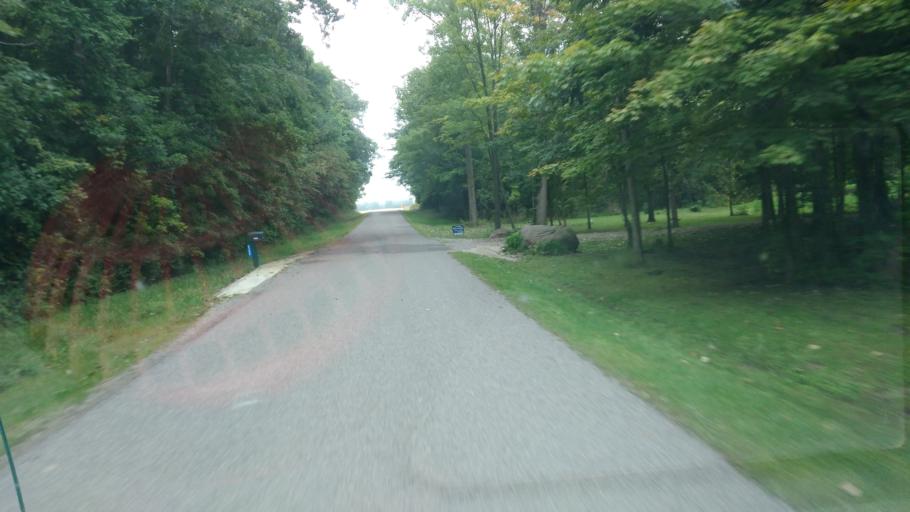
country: US
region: Ohio
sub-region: Logan County
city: Northwood
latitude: 40.4660
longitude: -83.5684
